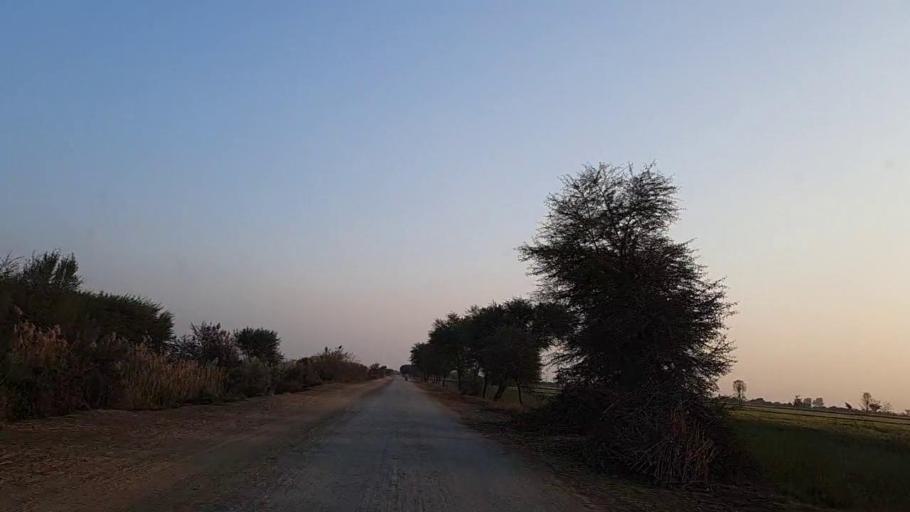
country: PK
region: Sindh
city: Shahdadpur
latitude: 25.9318
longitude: 68.5052
